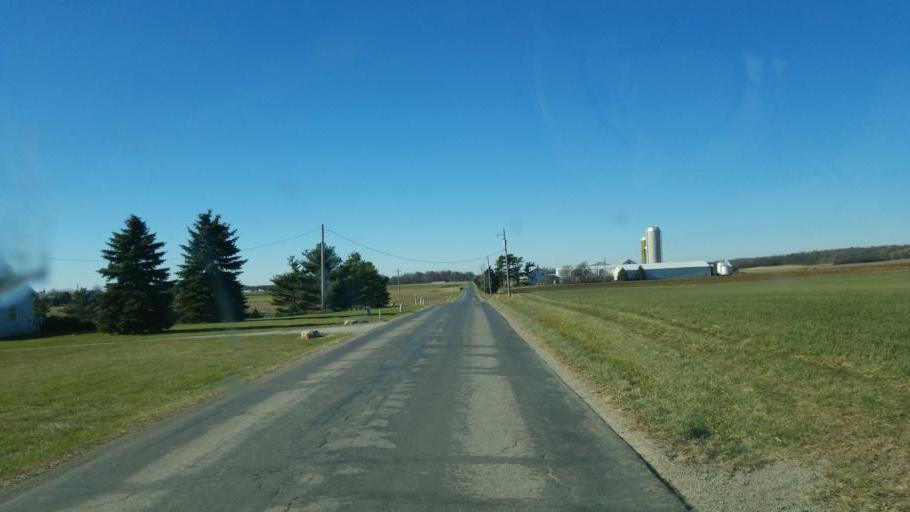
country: US
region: Ohio
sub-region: Huron County
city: Greenwich
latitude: 40.9605
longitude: -82.5534
